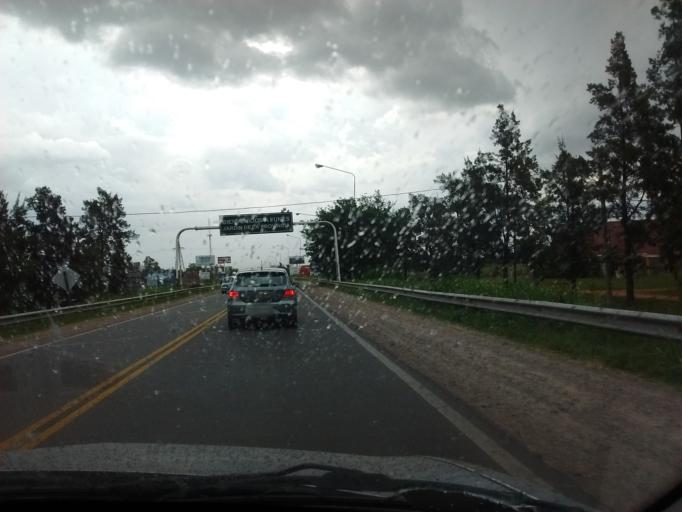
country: AR
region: Santa Fe
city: Funes
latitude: -32.9252
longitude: -60.7648
